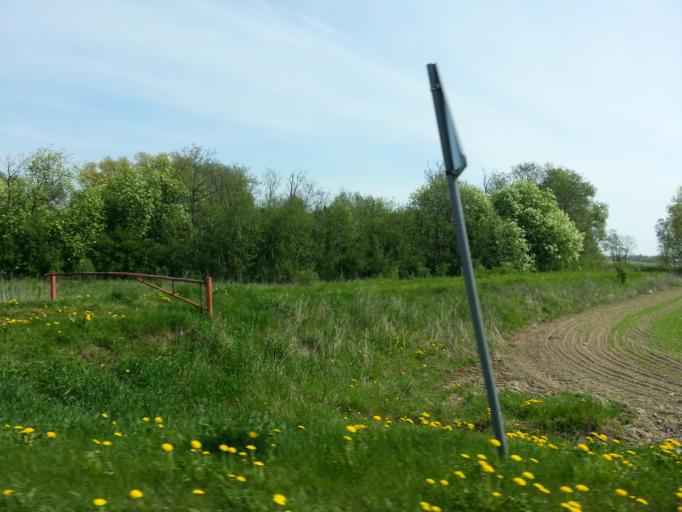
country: LT
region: Panevezys
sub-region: Panevezys City
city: Panevezys
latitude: 55.7952
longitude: 24.2779
